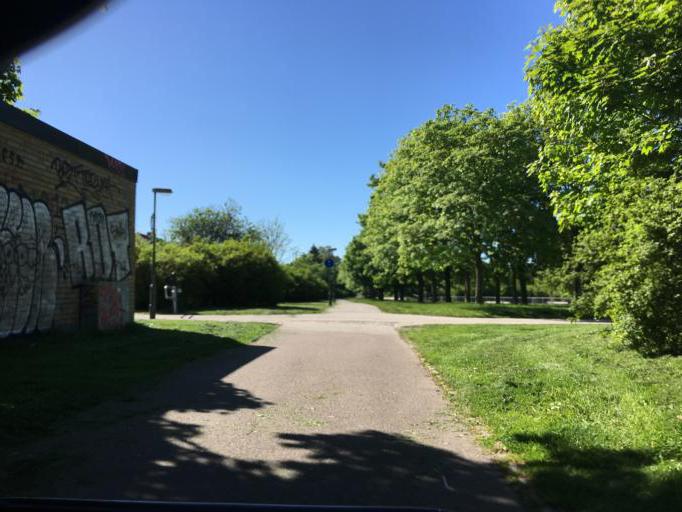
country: SE
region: Skane
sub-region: Malmo
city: Malmoe
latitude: 55.5806
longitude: 13.0419
